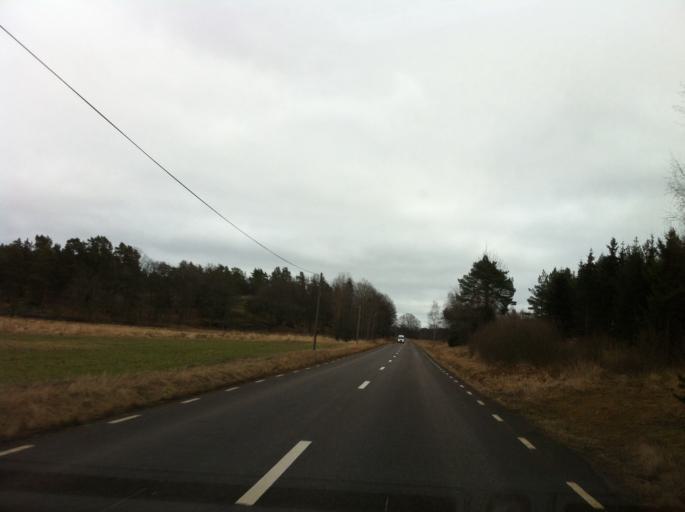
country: SE
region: Kalmar
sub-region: Vasterviks Kommun
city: Overum
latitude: 57.9120
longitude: 16.1646
